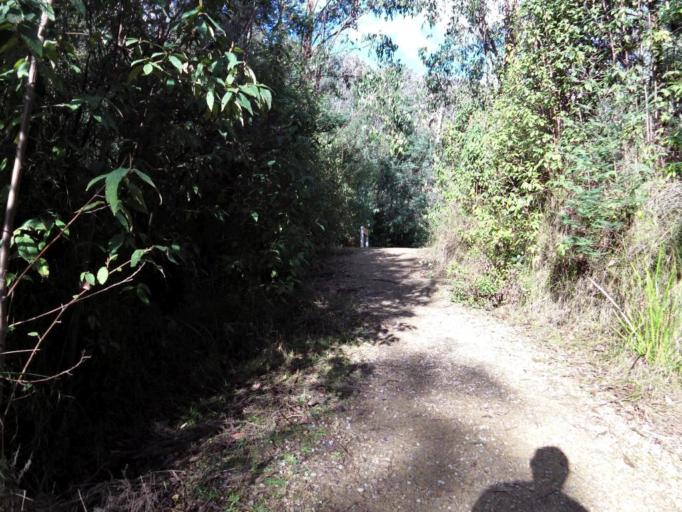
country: AU
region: Victoria
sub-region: Yarra Ranges
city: Millgrove
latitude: -37.5257
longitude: 145.7733
